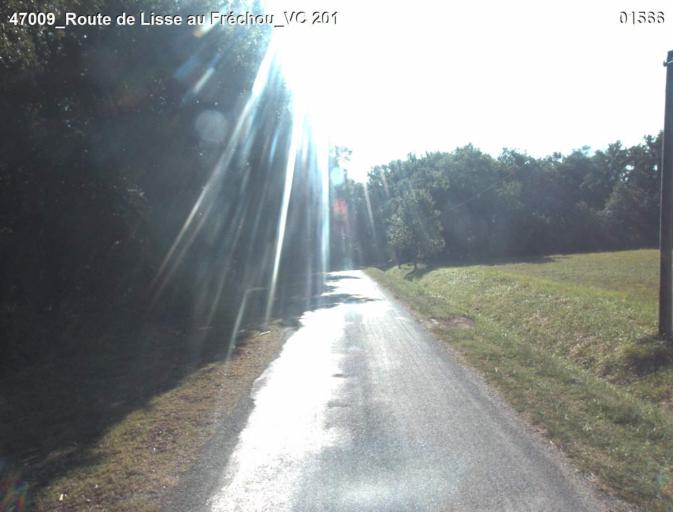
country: FR
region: Aquitaine
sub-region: Departement du Lot-et-Garonne
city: Mezin
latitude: 44.0929
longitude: 0.2929
